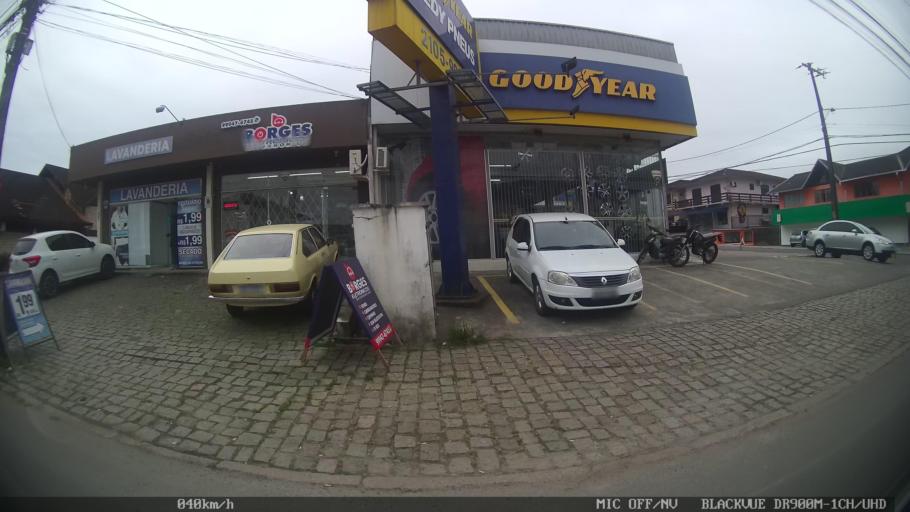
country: BR
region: Santa Catarina
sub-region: Joinville
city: Joinville
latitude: -26.2676
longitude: -48.8227
